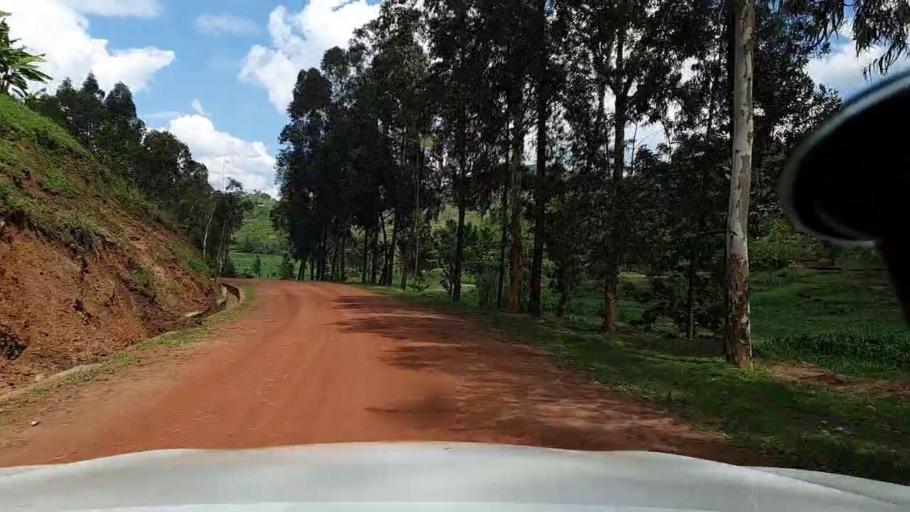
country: RW
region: Northern Province
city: Byumba
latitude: -1.7076
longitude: 29.8490
